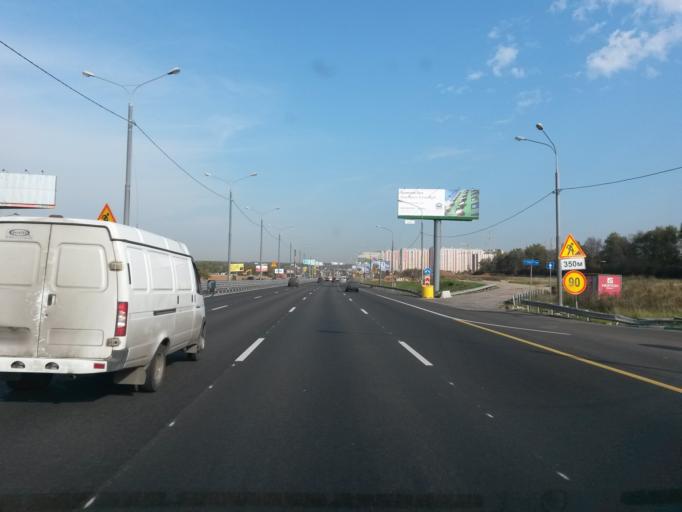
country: RU
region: Moskovskaya
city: Shcherbinka
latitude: 55.5201
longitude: 37.6094
